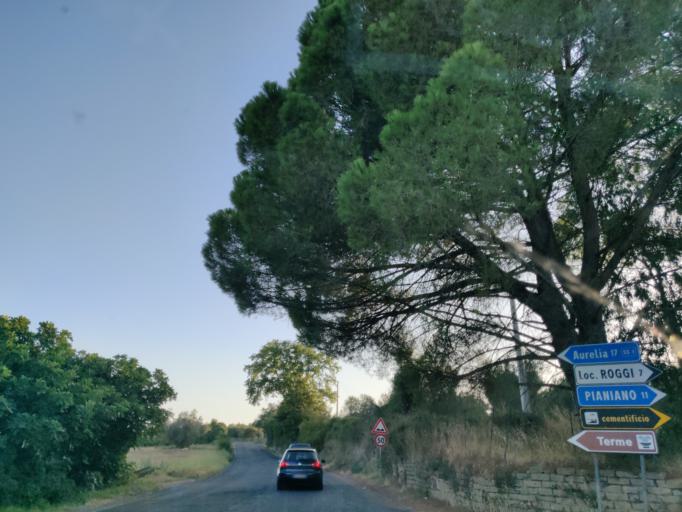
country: IT
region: Latium
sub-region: Provincia di Viterbo
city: Canino
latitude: 42.4536
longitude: 11.7388
